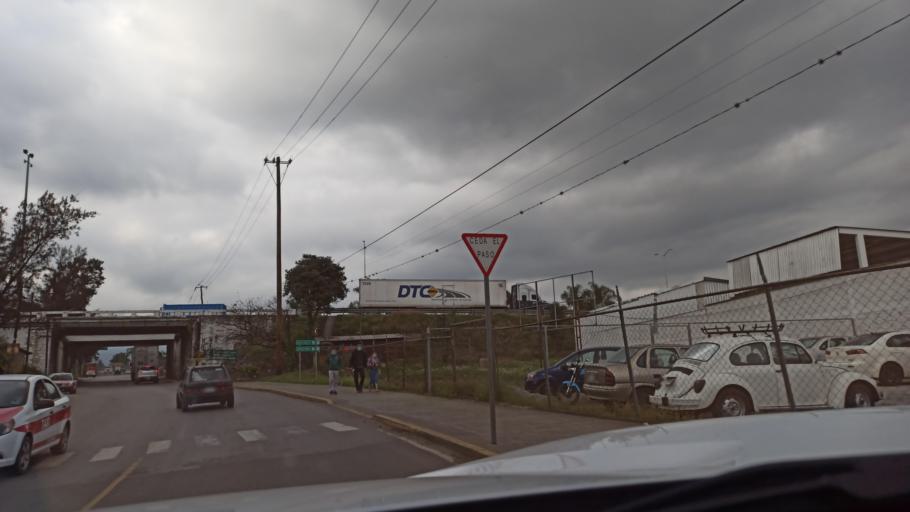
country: MX
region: Veracruz
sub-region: Fortin
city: Fortin de las Flores
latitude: 18.9069
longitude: -96.9975
